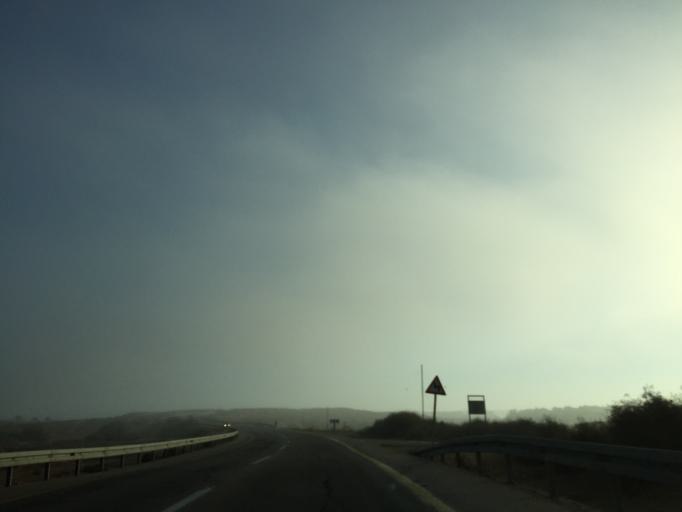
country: IL
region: Southern District
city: Yeroham
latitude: 30.9955
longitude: 34.9224
